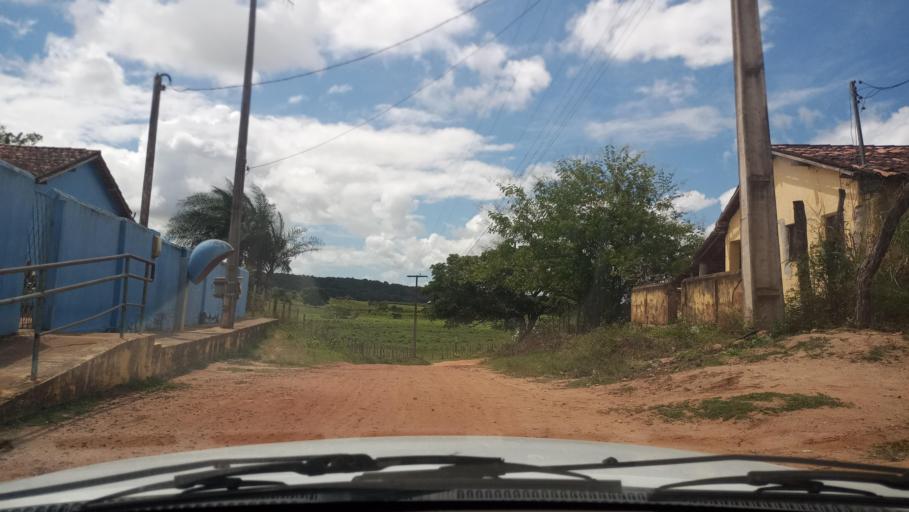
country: BR
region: Rio Grande do Norte
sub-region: Goianinha
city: Goianinha
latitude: -6.2617
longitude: -35.2567
